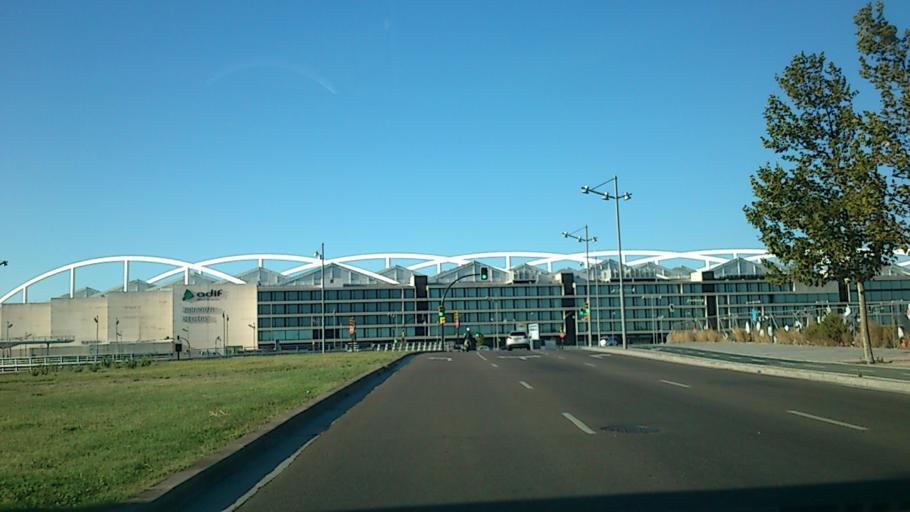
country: ES
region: Aragon
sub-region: Provincia de Zaragoza
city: Almozara
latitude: 41.6612
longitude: -0.9086
